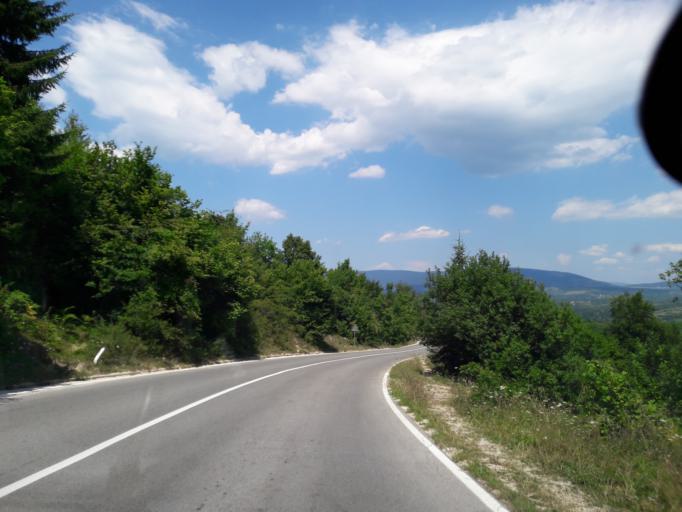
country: BA
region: Republika Srpska
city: Sipovo
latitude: 44.1306
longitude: 17.1787
